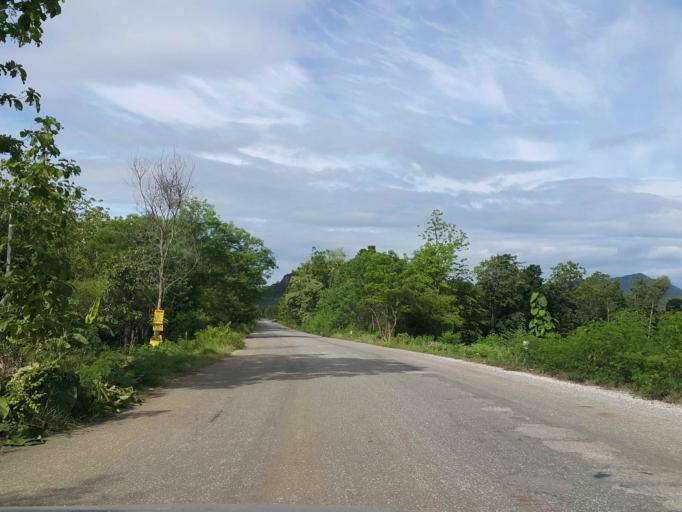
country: TH
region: Sukhothai
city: Thung Saliam
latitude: 17.2632
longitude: 99.5327
